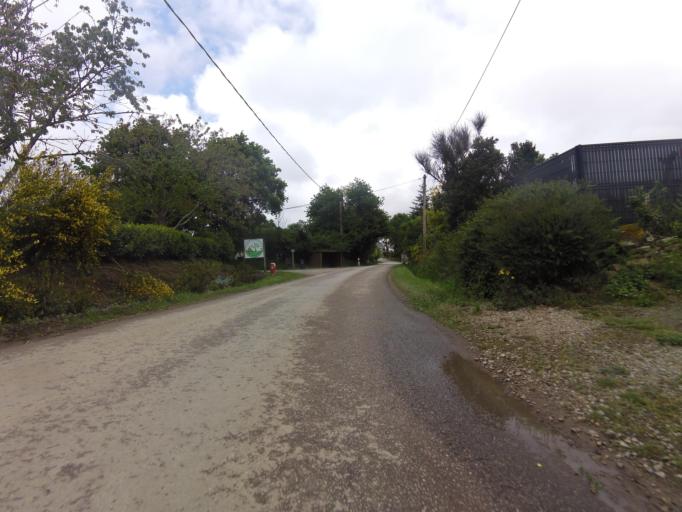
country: FR
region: Brittany
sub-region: Departement du Morbihan
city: Plougoumelen
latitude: 47.6425
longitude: -2.8973
